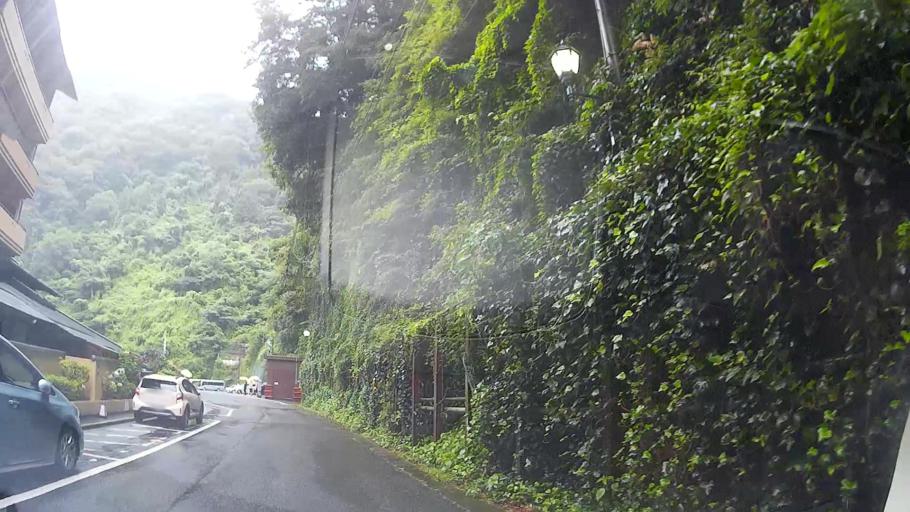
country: JP
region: Oita
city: Tsukawaki
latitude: 33.1860
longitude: 131.0313
